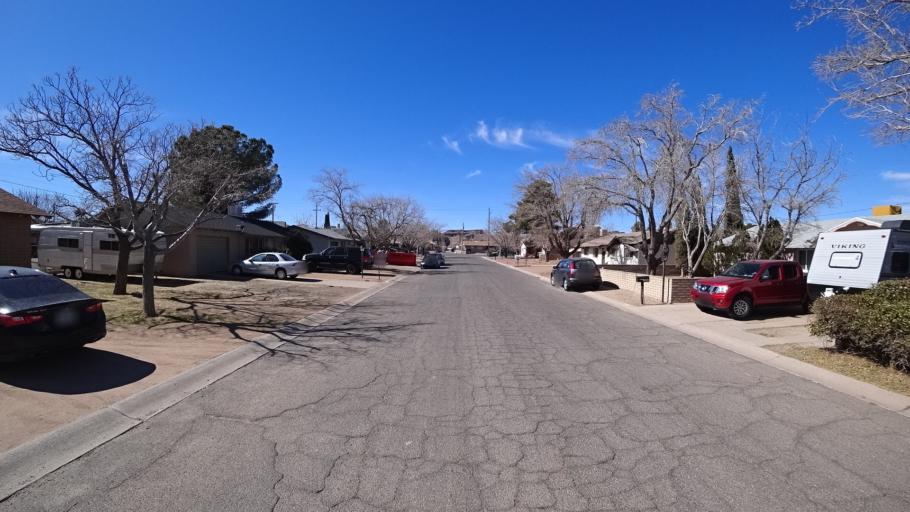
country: US
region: Arizona
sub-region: Mohave County
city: Kingman
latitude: 35.2125
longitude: -114.0390
